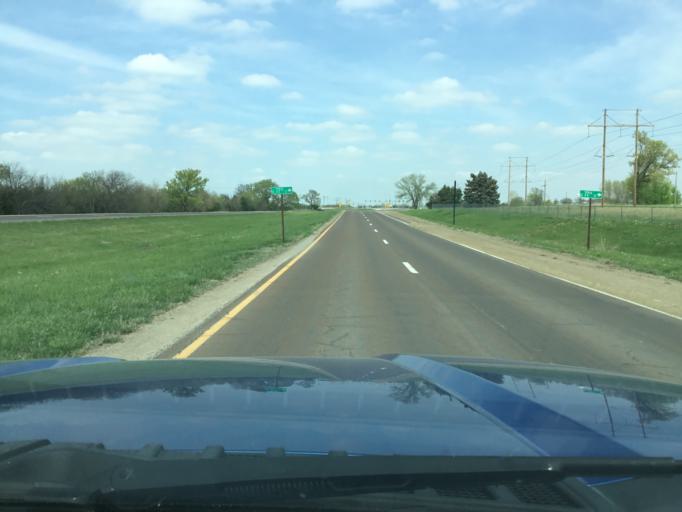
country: US
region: Kansas
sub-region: Osage County
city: Carbondale
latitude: 38.9309
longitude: -95.6875
